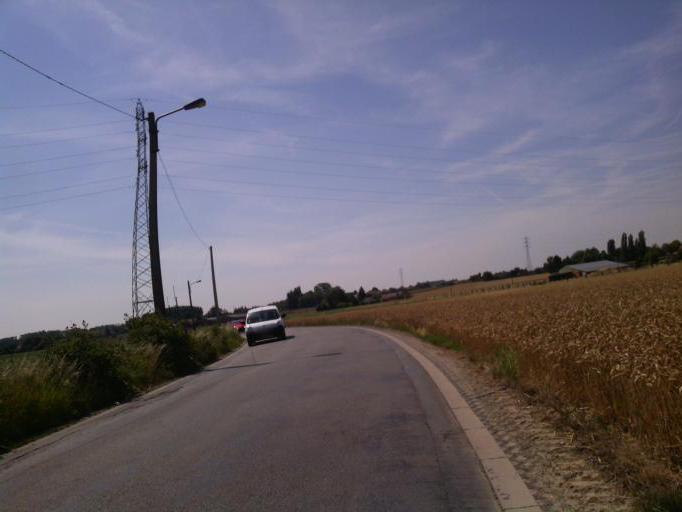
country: BE
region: Wallonia
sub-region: Province du Hainaut
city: Pecq
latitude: 50.6360
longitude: 3.3360
